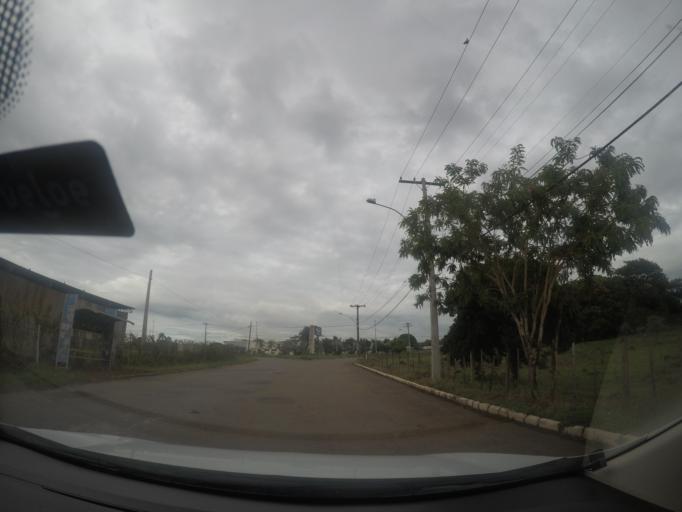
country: BR
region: Goias
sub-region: Goiania
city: Goiania
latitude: -16.6386
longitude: -49.3420
